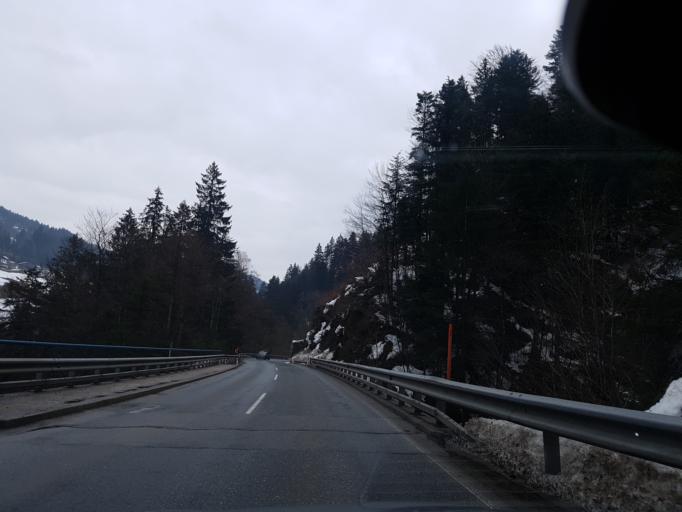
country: AT
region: Tyrol
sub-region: Politischer Bezirk Kufstein
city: Worgl
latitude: 47.4707
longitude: 12.0787
